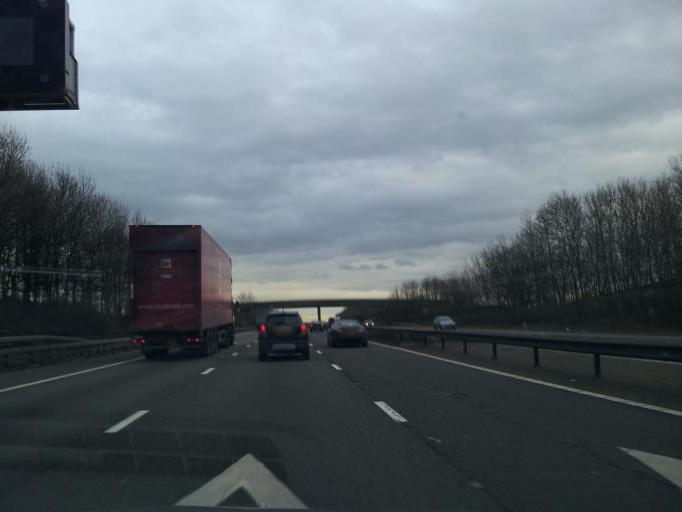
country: GB
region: England
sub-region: Warwickshire
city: Long Lawford
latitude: 52.4276
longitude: -1.3191
